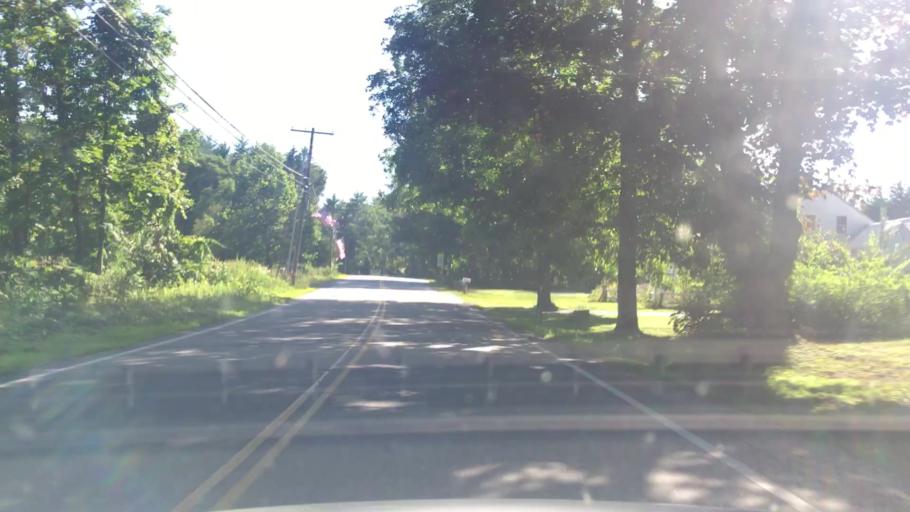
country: US
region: New Hampshire
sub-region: Rockingham County
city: Brentwood
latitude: 42.9849
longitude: -71.0638
